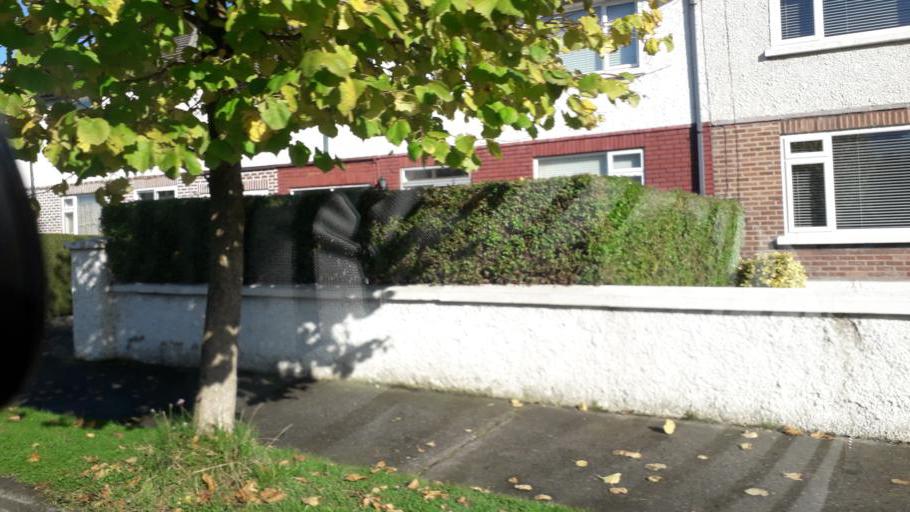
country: IE
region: Leinster
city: Raheny
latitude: 53.3797
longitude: -6.1808
